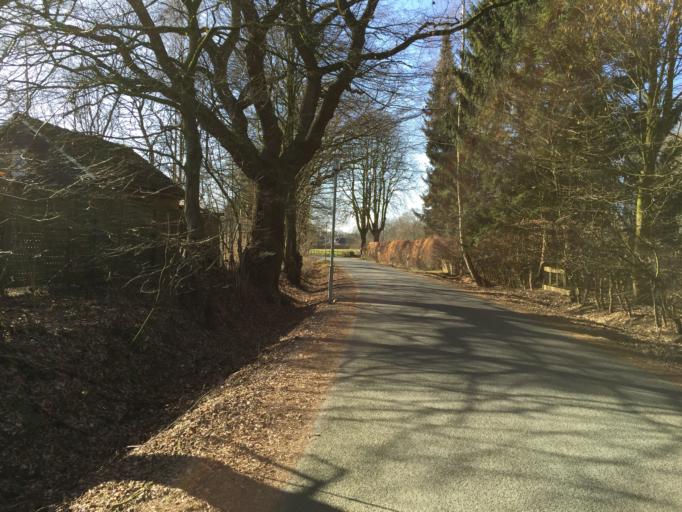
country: DE
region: Lower Saxony
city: Oldenburg
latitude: 53.1710
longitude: 8.2419
